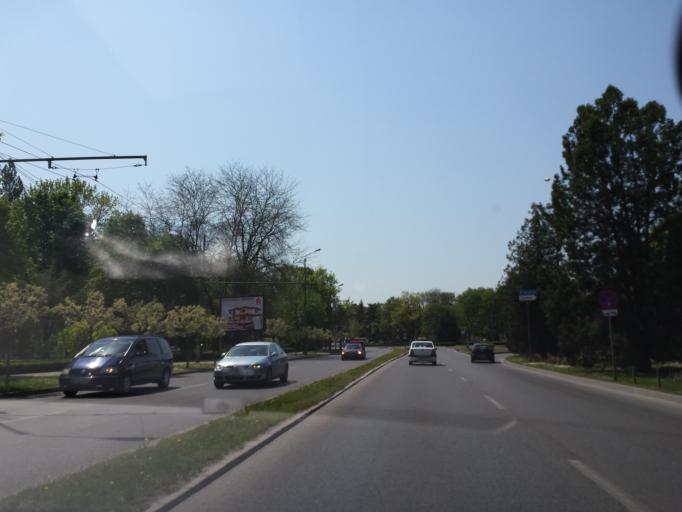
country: RO
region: Timis
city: Timisoara
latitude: 45.7544
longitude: 21.2330
